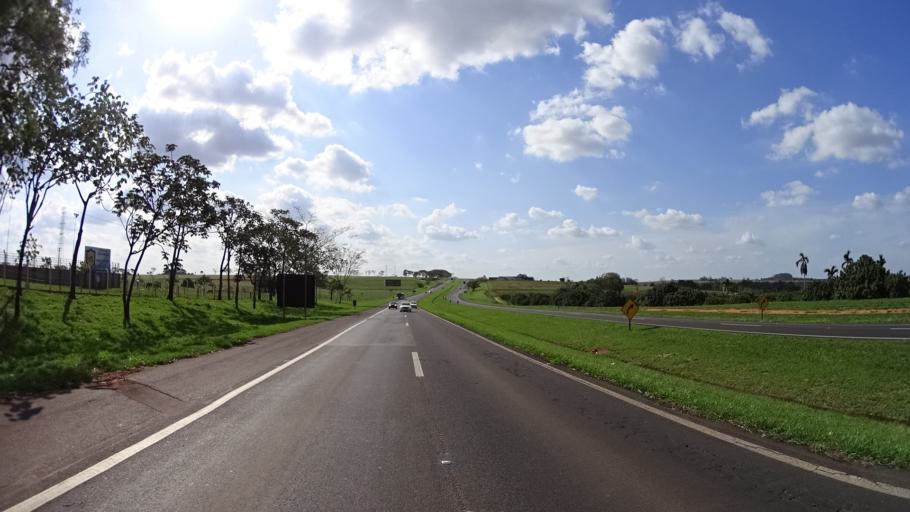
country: BR
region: Sao Paulo
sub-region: Guapiacu
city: Guapiacu
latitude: -20.9584
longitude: -49.2474
